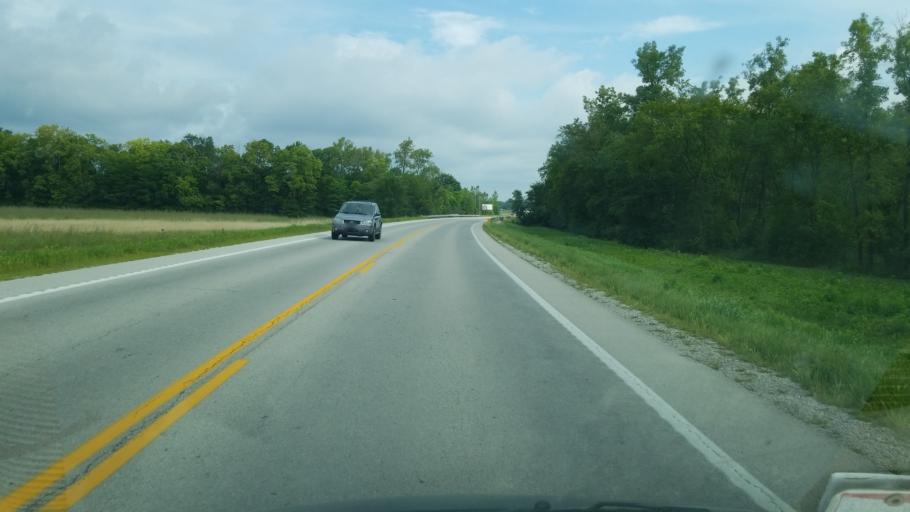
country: US
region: Ohio
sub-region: Sandusky County
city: Ballville
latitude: 41.2880
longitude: -83.1716
